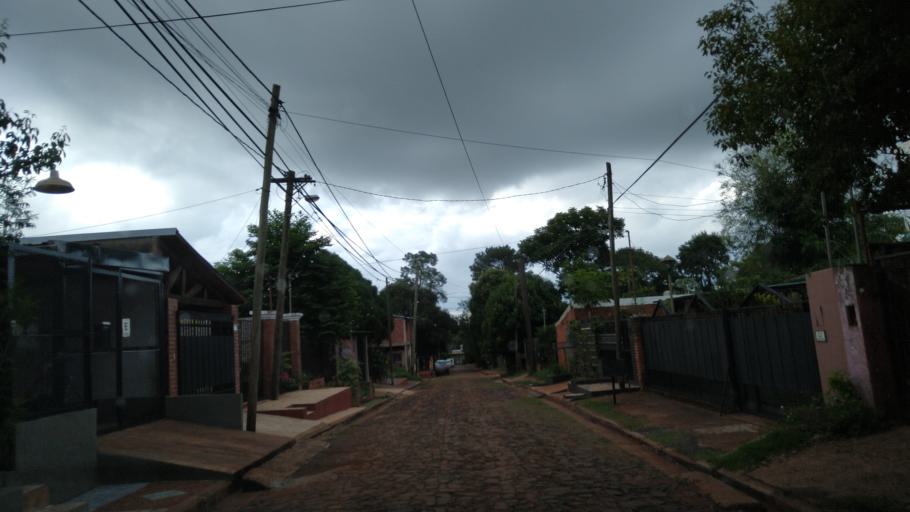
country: AR
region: Misiones
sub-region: Departamento de Capital
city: Posadas
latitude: -27.4121
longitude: -55.9039
